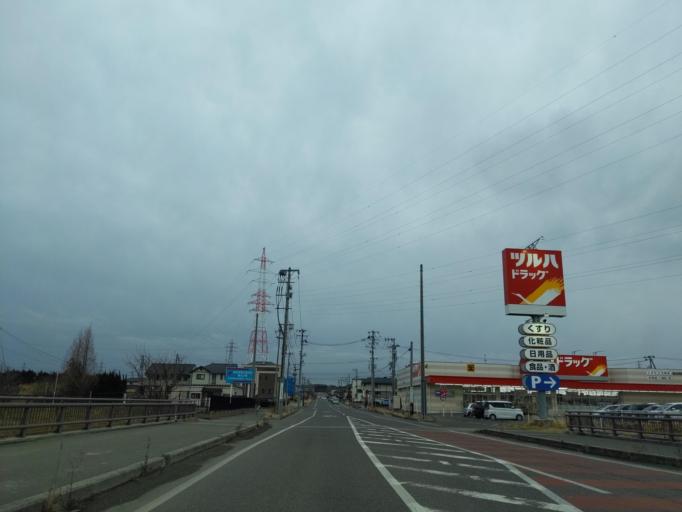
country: JP
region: Fukushima
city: Koriyama
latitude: 37.4460
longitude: 140.3844
